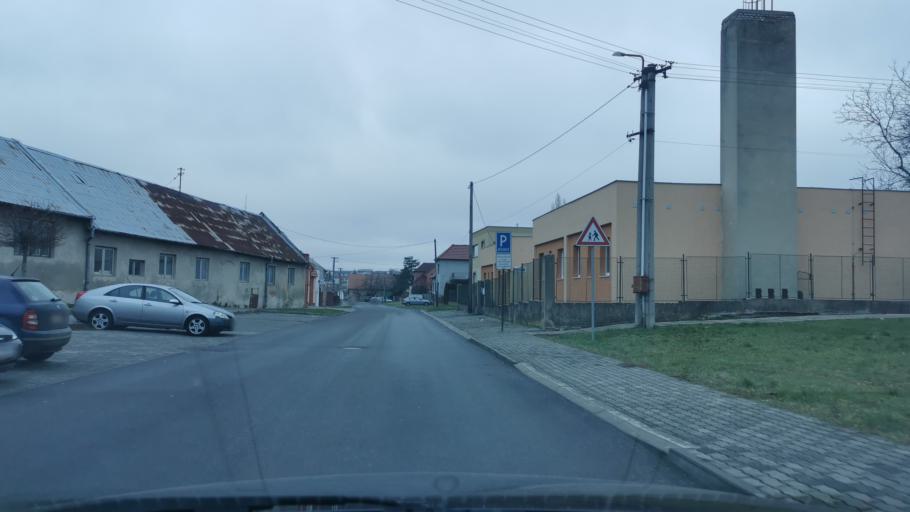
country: SK
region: Trnavsky
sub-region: Okres Skalica
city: Skalica
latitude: 48.8492
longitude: 17.2296
